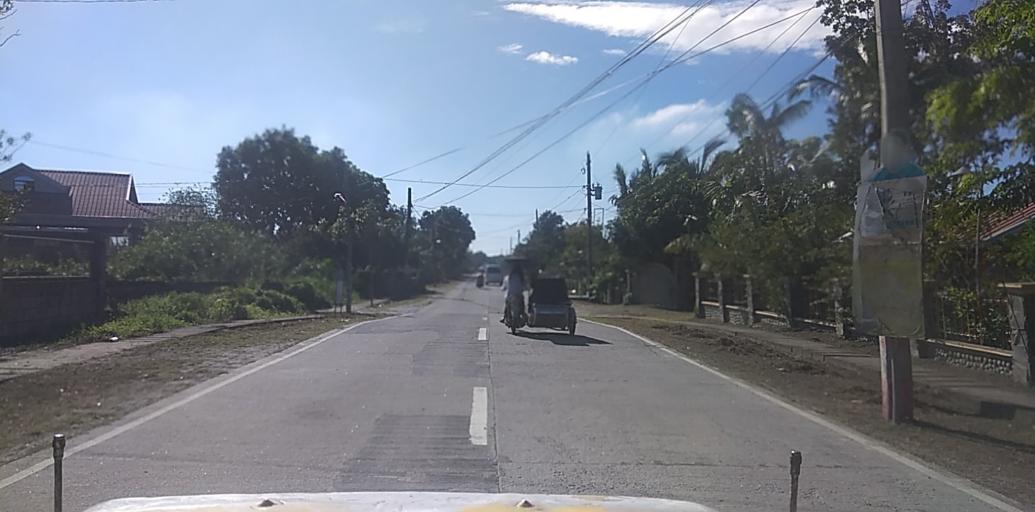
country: PH
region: Central Luzon
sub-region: Province of Pampanga
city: Mexico
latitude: 15.0812
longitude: 120.7167
